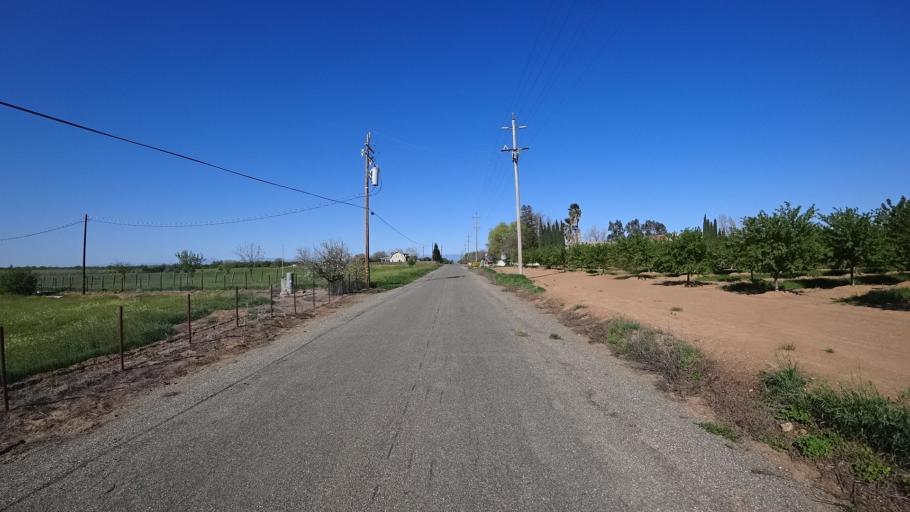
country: US
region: California
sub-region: Glenn County
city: Hamilton City
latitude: 39.7757
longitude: -122.0967
